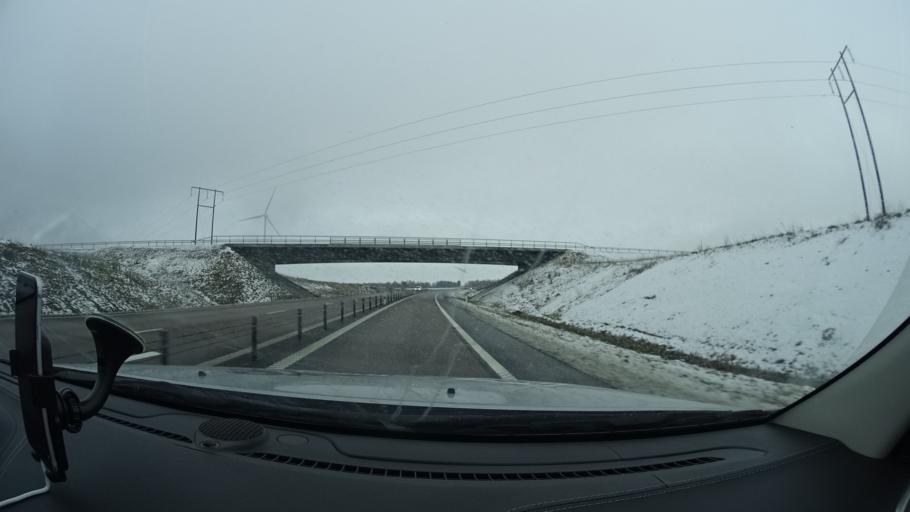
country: SE
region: OEstergoetland
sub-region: Motala Kommun
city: Stenstorp
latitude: 58.4735
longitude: 15.0430
